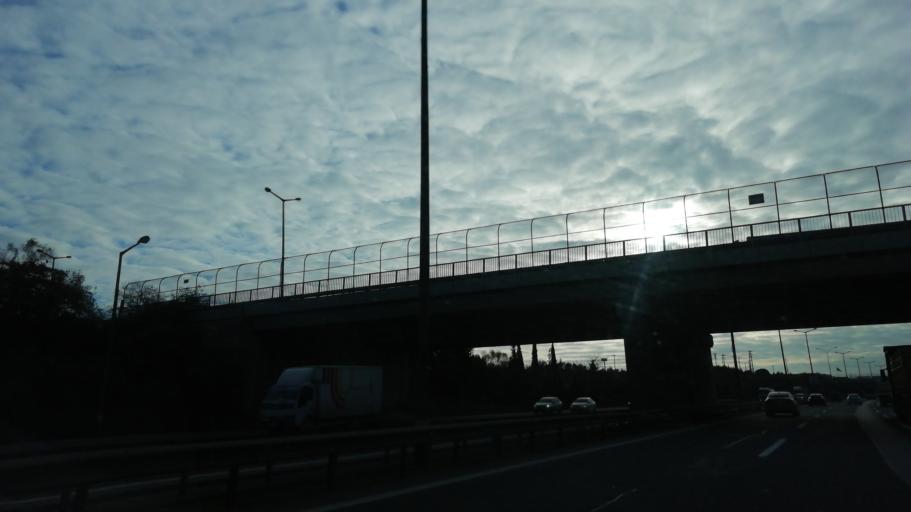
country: TR
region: Kocaeli
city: Balcik
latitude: 40.8709
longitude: 29.3954
